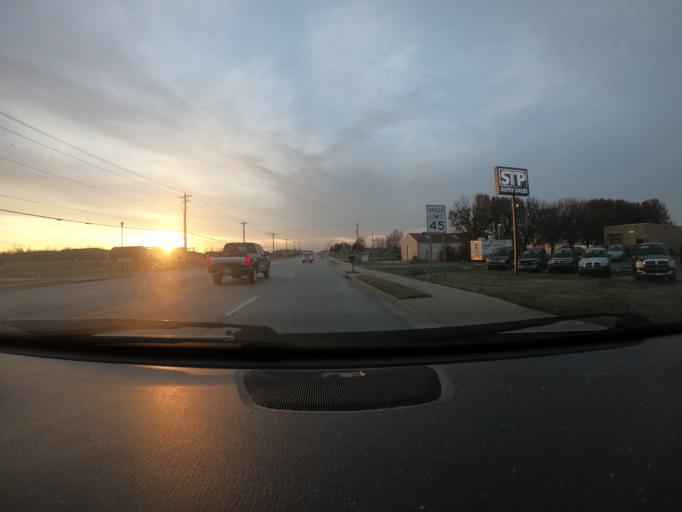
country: US
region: Arkansas
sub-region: Benton County
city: Bentonville
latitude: 36.3356
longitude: -94.2116
